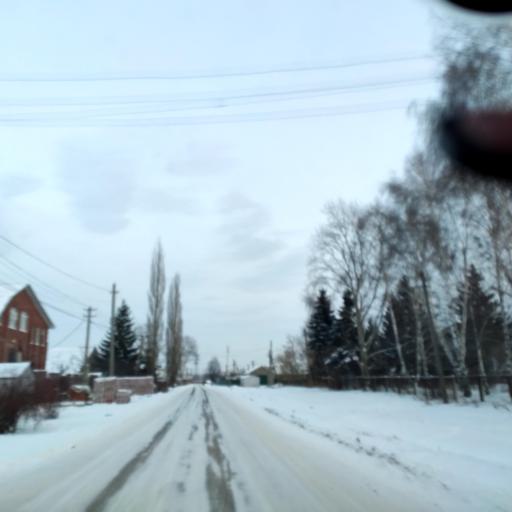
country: RU
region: Bashkortostan
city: Mikhaylovka
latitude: 54.8704
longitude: 55.7309
